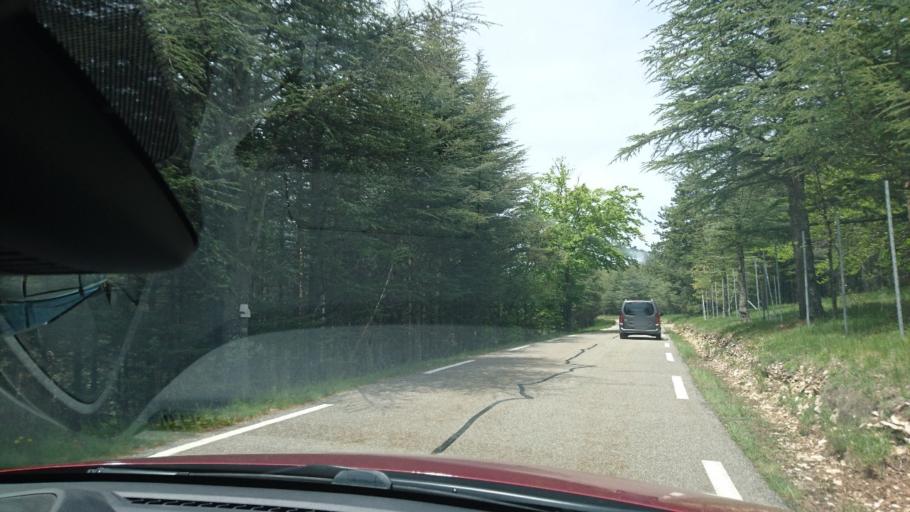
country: FR
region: Provence-Alpes-Cote d'Azur
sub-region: Departement du Vaucluse
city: Sault
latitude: 44.1362
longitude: 5.3695
